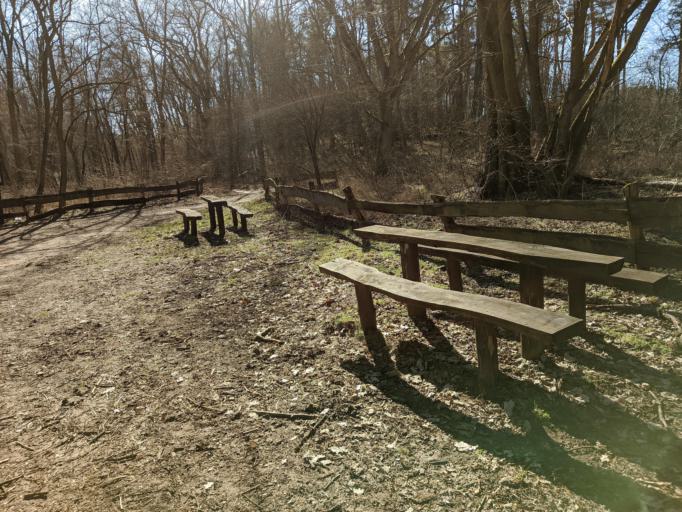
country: PL
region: Lubusz
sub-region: Powiat miedzyrzecki
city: Bledzew
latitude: 52.5769
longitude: 15.4302
